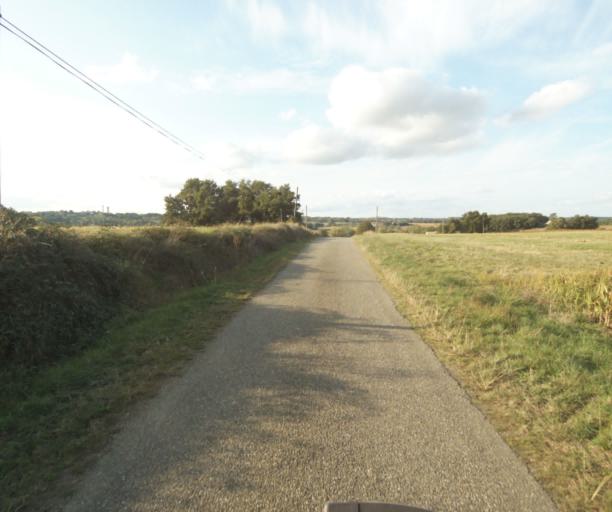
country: FR
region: Midi-Pyrenees
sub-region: Departement de la Haute-Garonne
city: Launac
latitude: 43.8164
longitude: 1.1362
